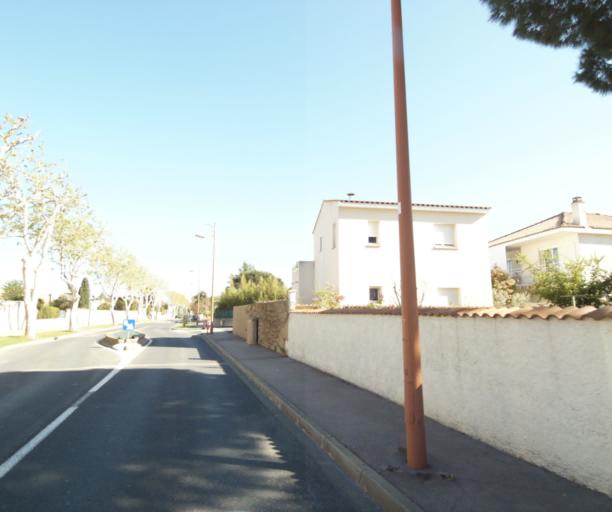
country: FR
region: Languedoc-Roussillon
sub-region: Departement de l'Herault
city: Perols
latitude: 43.5674
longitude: 3.9479
